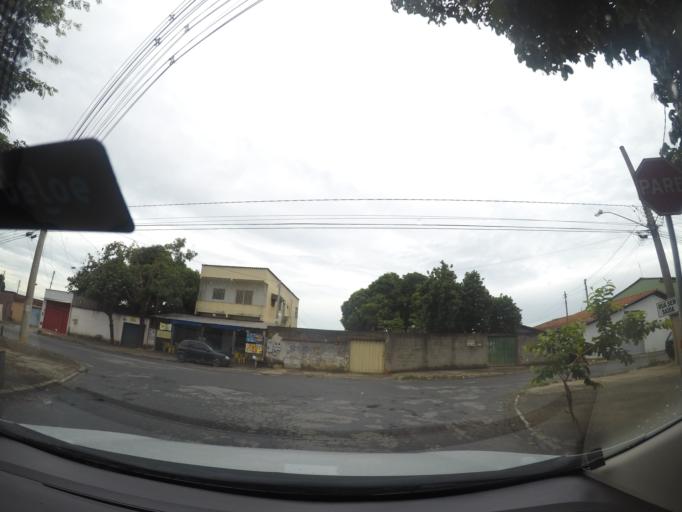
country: BR
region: Goias
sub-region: Goiania
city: Goiania
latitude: -16.6812
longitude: -49.2359
